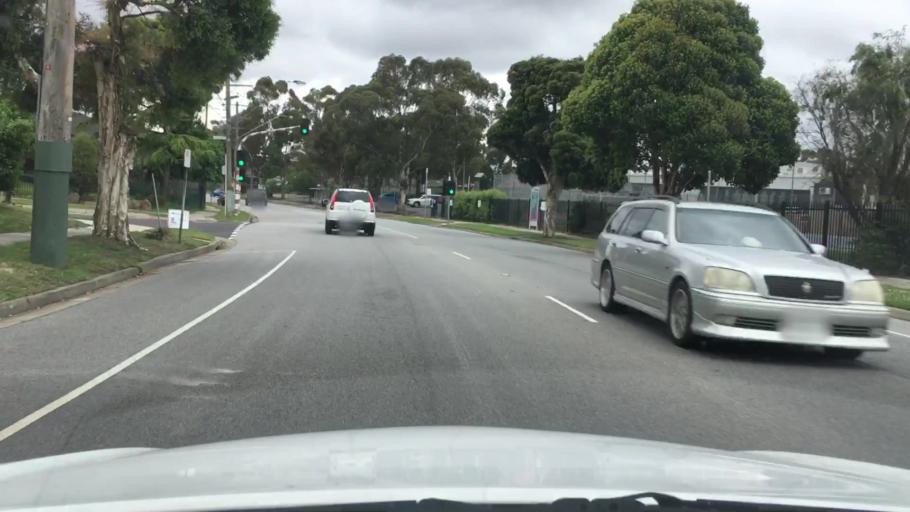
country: AU
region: Victoria
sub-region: Greater Dandenong
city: Noble Park North
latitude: -37.9491
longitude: 145.1920
